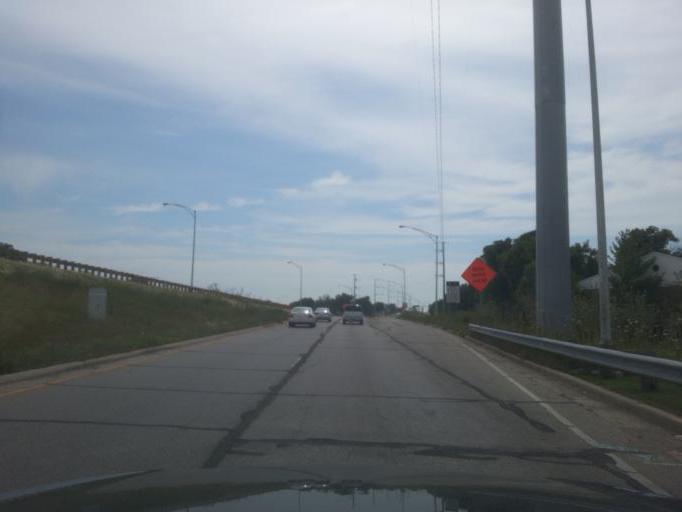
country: US
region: Wisconsin
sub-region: Dane County
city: Shorewood Hills
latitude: 43.0457
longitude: -89.4728
